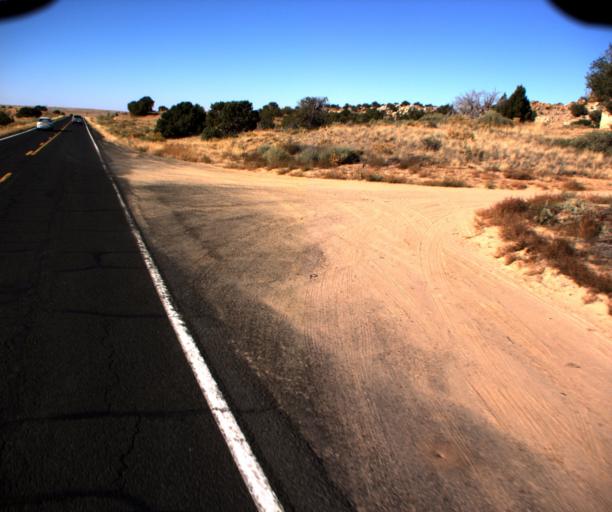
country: US
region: Arizona
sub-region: Navajo County
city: First Mesa
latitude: 35.8332
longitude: -110.2690
